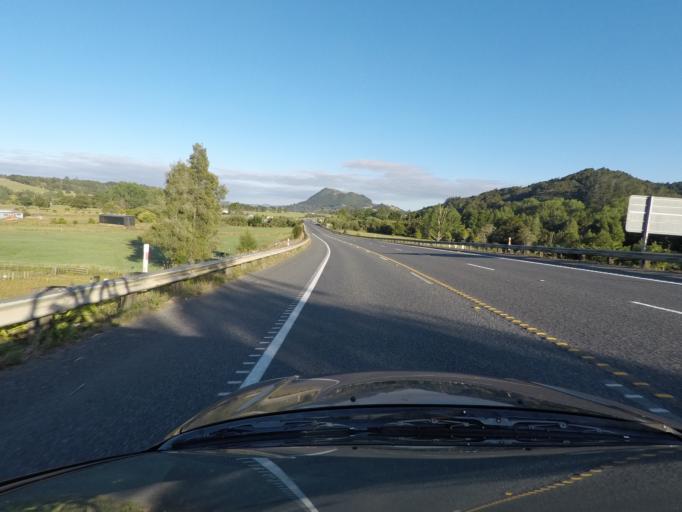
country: NZ
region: Northland
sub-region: Whangarei
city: Whangarei
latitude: -35.6270
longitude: 174.2950
